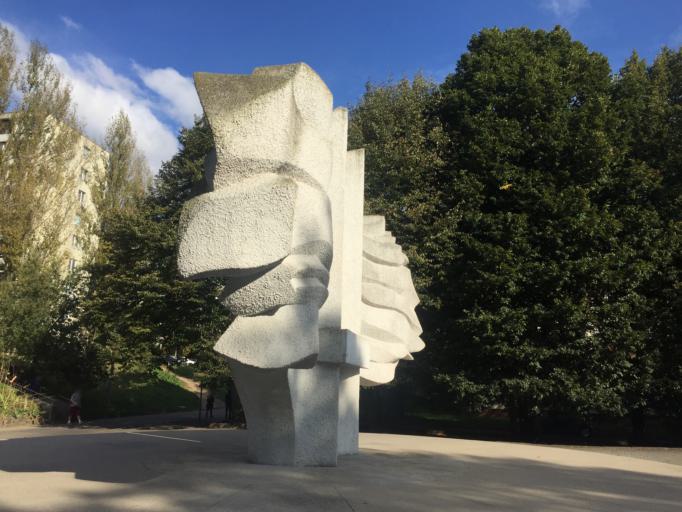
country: RU
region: Kaliningrad
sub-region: Gorod Kaliningrad
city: Kaliningrad
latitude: 54.6958
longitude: 20.5096
